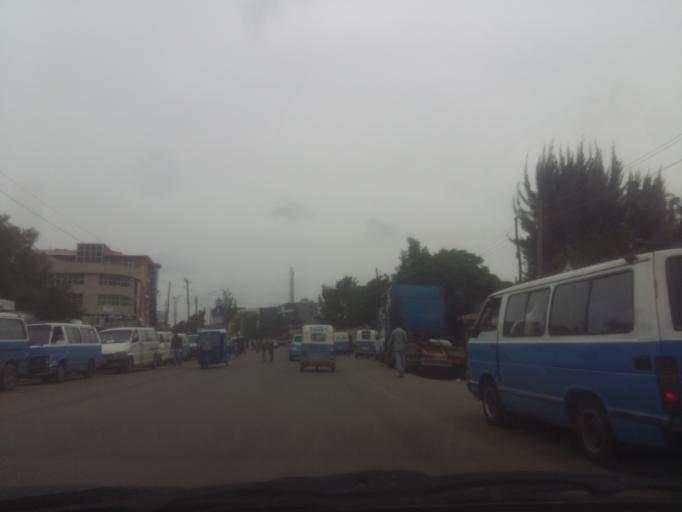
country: ET
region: Oromiya
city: Bishoftu
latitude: 8.7918
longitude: 38.9051
